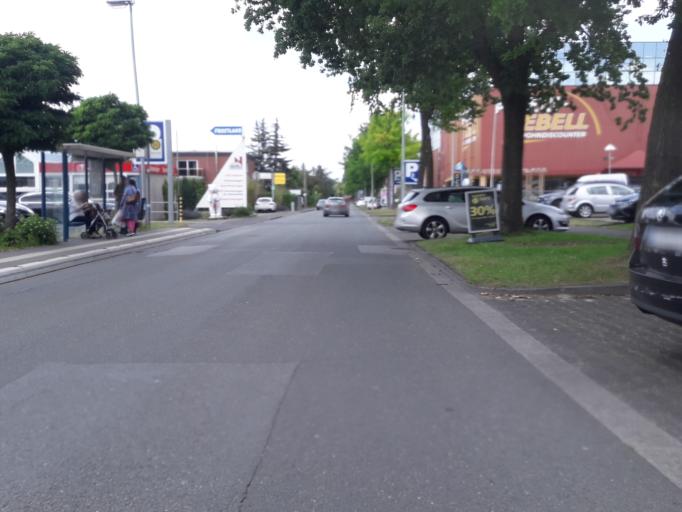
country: DE
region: North Rhine-Westphalia
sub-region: Regierungsbezirk Detmold
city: Paderborn
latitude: 51.7345
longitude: 8.7888
